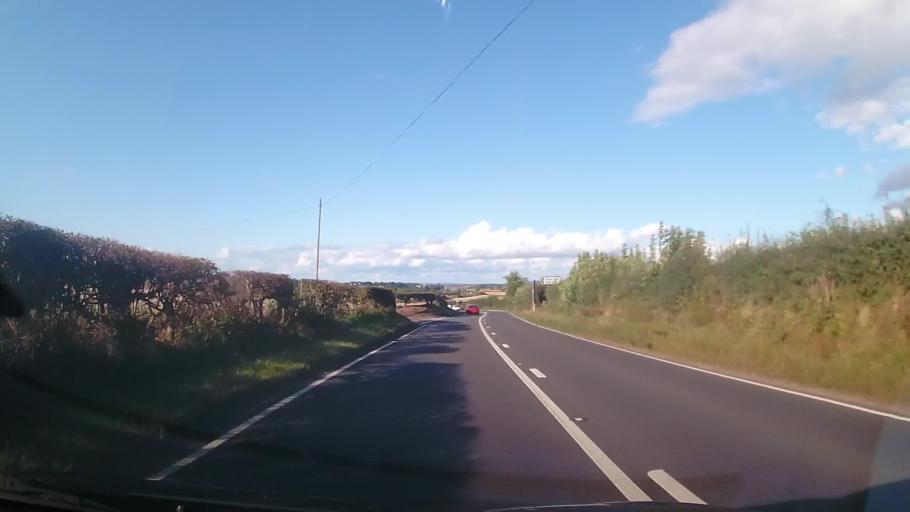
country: GB
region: England
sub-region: Shropshire
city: Bayston Hill
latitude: 52.6535
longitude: -2.7692
